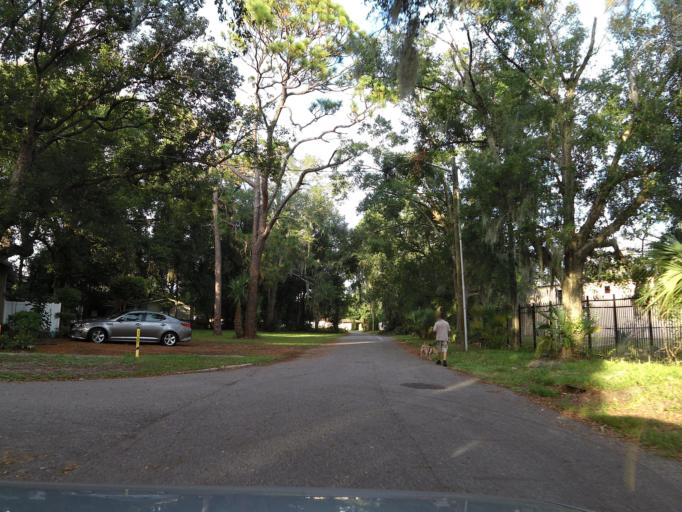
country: US
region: Florida
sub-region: Duval County
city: Jacksonville
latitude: 30.3695
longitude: -81.6537
